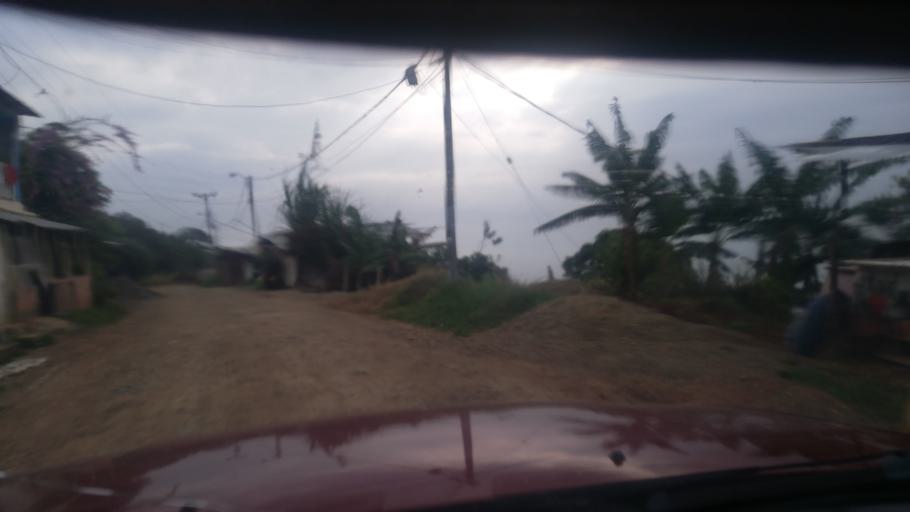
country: CO
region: Valle del Cauca
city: Cali
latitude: 3.5055
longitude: -76.5442
